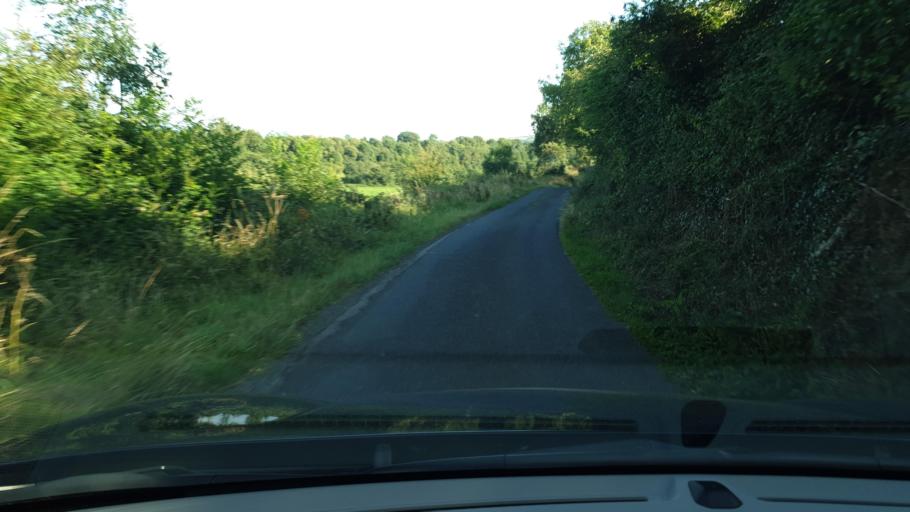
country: IE
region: Leinster
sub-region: An Mhi
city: Stamullin
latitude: 53.6067
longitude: -6.2738
